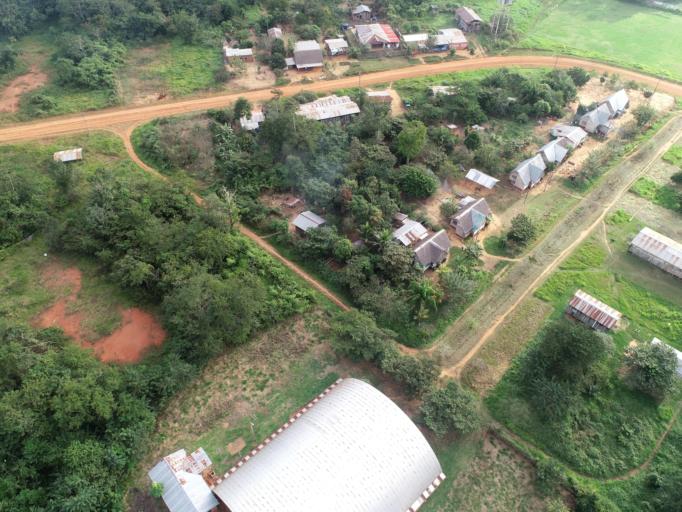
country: PE
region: Madre de Dios
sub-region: Provincia de Tambopata
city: Puerto Maldonado
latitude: -12.1975
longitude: -68.6323
